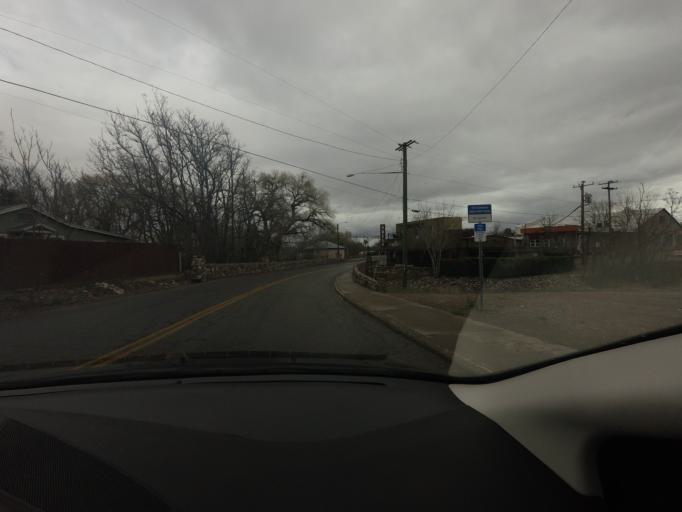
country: US
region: Arizona
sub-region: Yavapai County
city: Cottonwood
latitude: 34.7499
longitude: -112.0280
